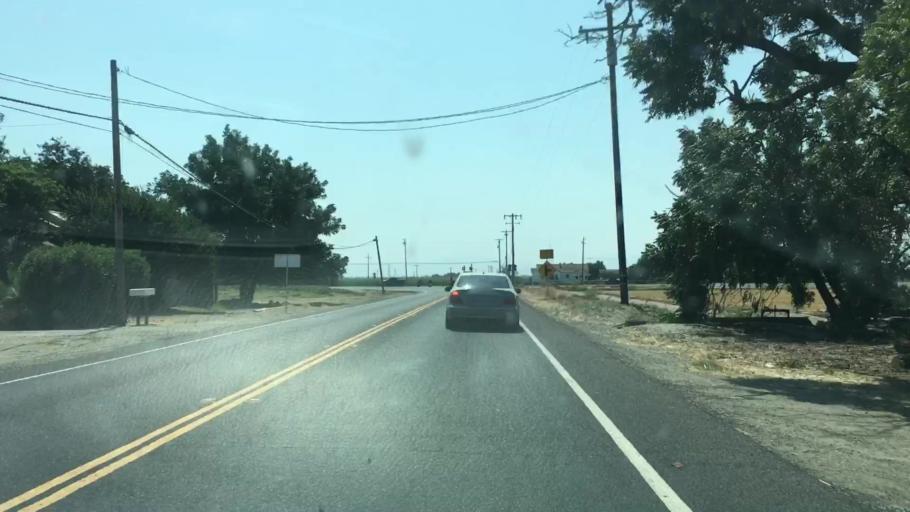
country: US
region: California
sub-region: San Joaquin County
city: Tracy
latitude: 37.7921
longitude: -121.4477
